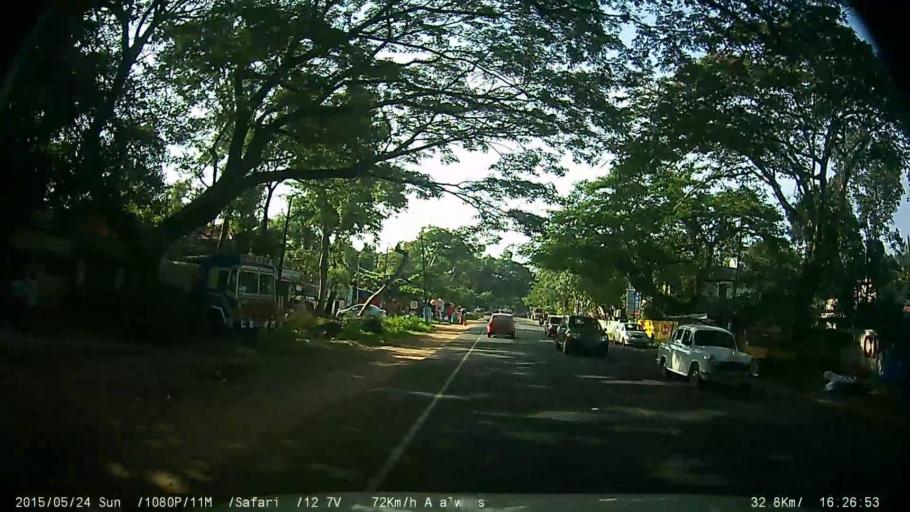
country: IN
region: Kerala
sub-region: Alappuzha
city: Alleppey
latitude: 9.5230
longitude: 76.3276
